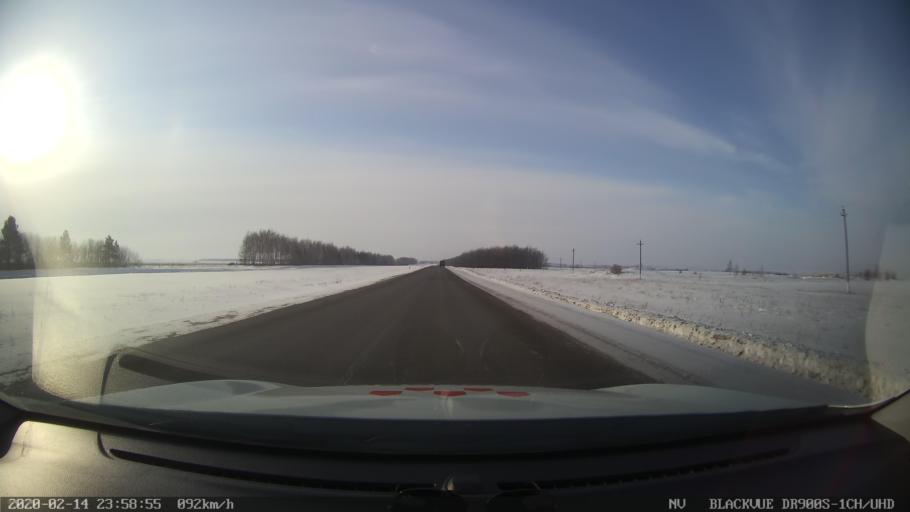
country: RU
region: Tatarstan
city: Kuybyshevskiy Zaton
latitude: 55.3422
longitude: 49.0765
